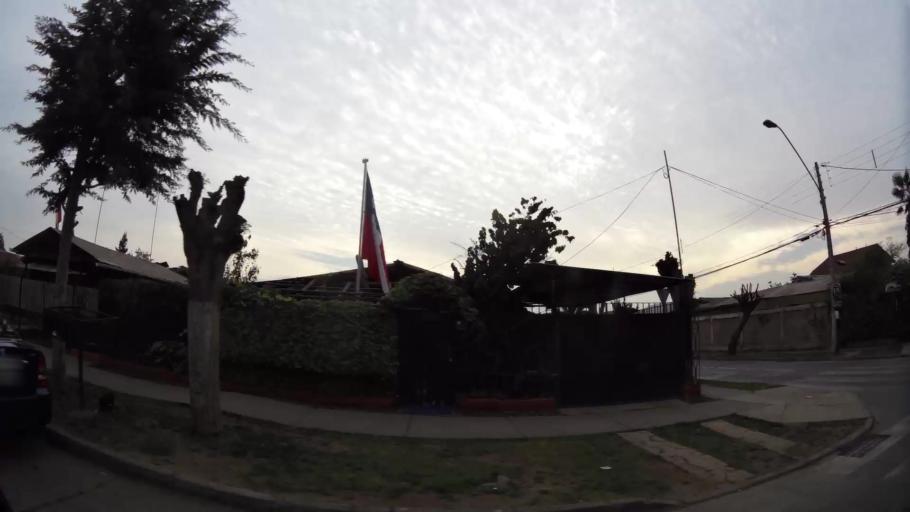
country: CL
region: Santiago Metropolitan
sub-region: Provincia de Santiago
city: Lo Prado
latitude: -33.5152
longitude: -70.7690
